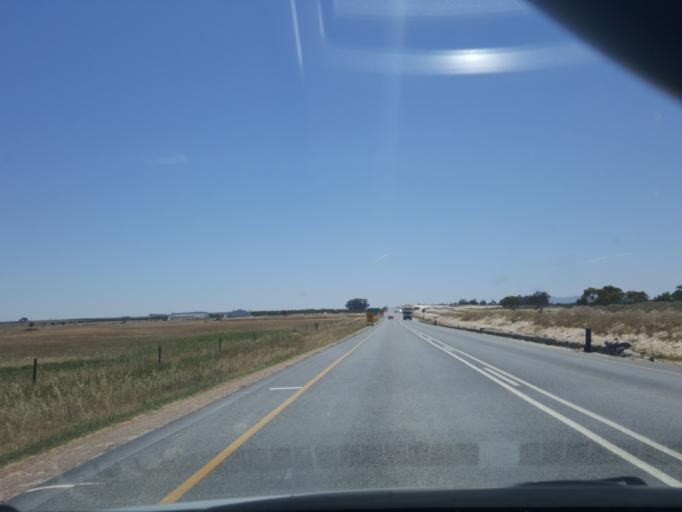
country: ZA
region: Western Cape
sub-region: City of Cape Town
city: Atlantis
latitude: -33.5728
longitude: 18.6181
